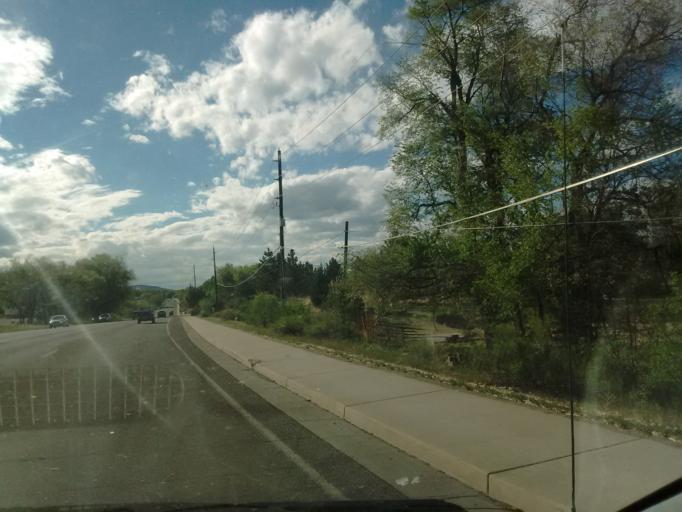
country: US
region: Colorado
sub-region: Mesa County
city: Redlands
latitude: 39.0644
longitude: -108.5952
